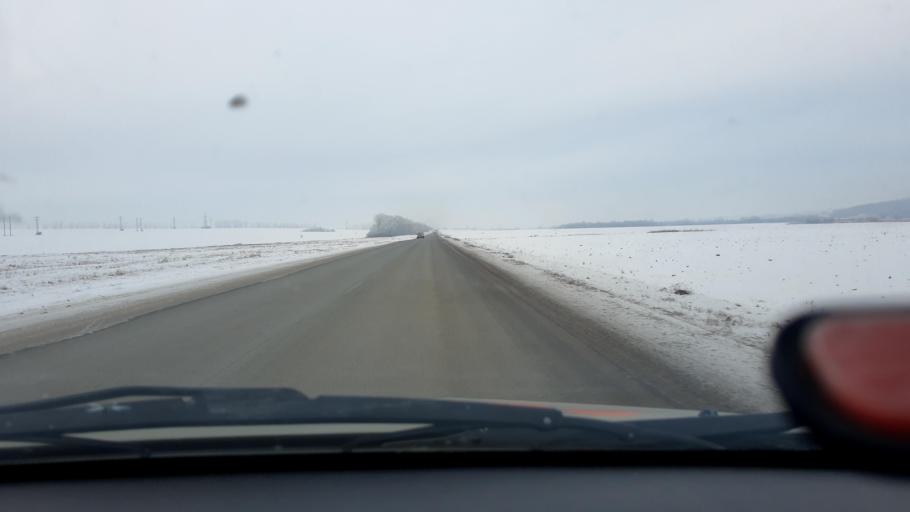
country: RU
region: Bashkortostan
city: Avdon
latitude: 54.3851
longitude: 55.8053
